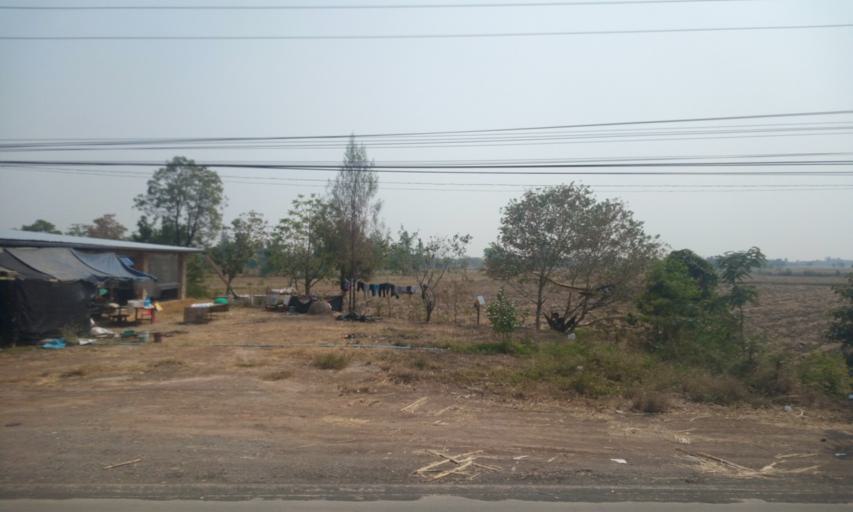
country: TH
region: Nakhon Ratchasima
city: Phimai
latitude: 15.3254
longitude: 102.4365
